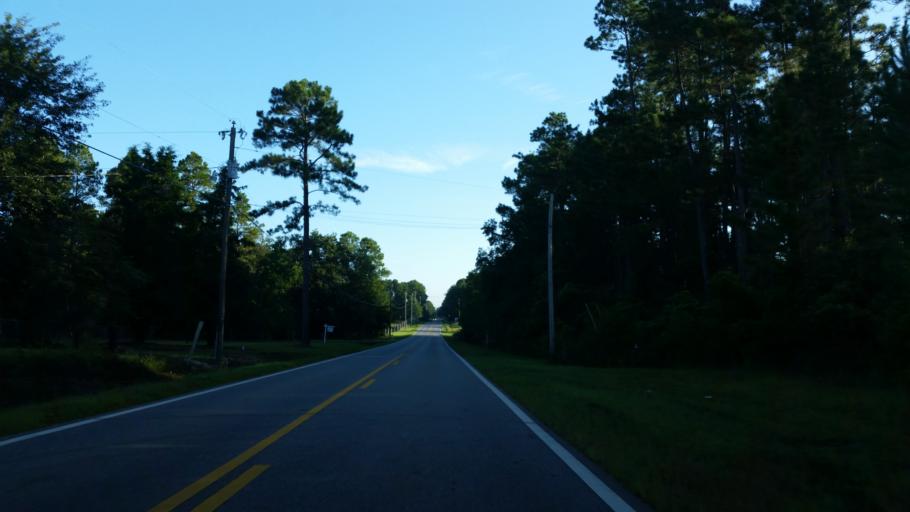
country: US
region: Florida
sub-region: Escambia County
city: Bellview
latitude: 30.5080
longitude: -87.3225
